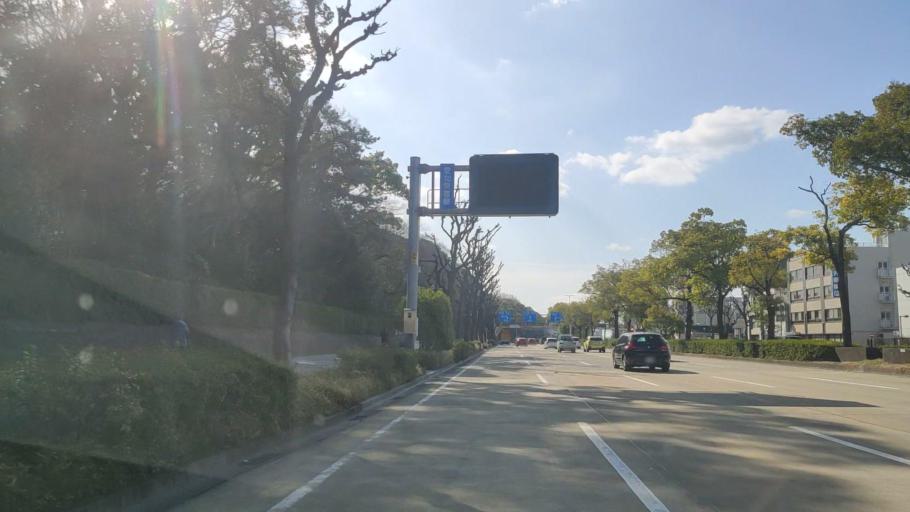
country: JP
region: Aichi
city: Nagoya-shi
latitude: 35.1270
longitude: 136.9070
